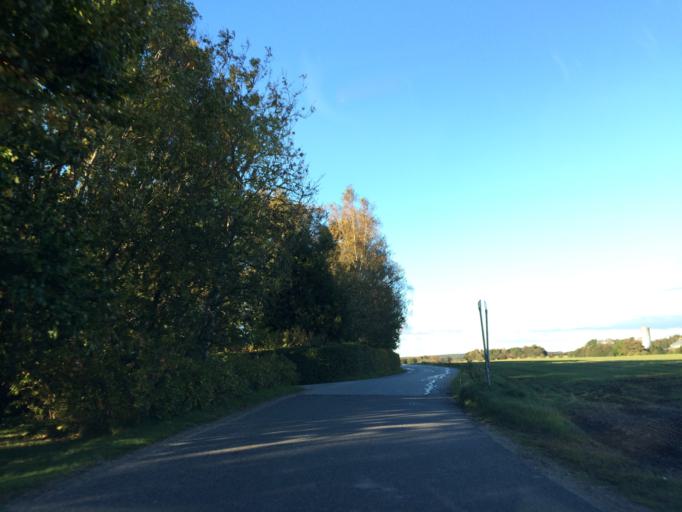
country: DK
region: Central Jutland
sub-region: Silkeborg Kommune
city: Svejbaek
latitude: 56.1698
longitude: 9.6933
